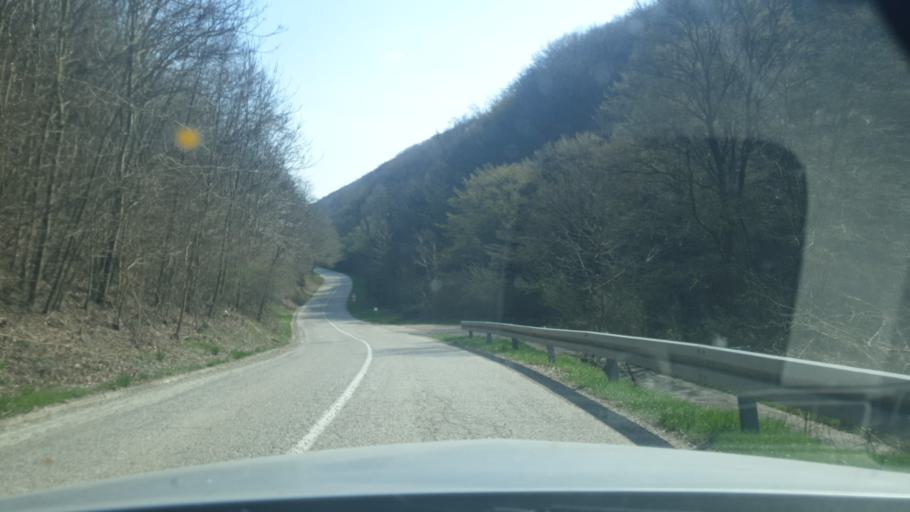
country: RS
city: Vrdnik
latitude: 45.1436
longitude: 19.7714
